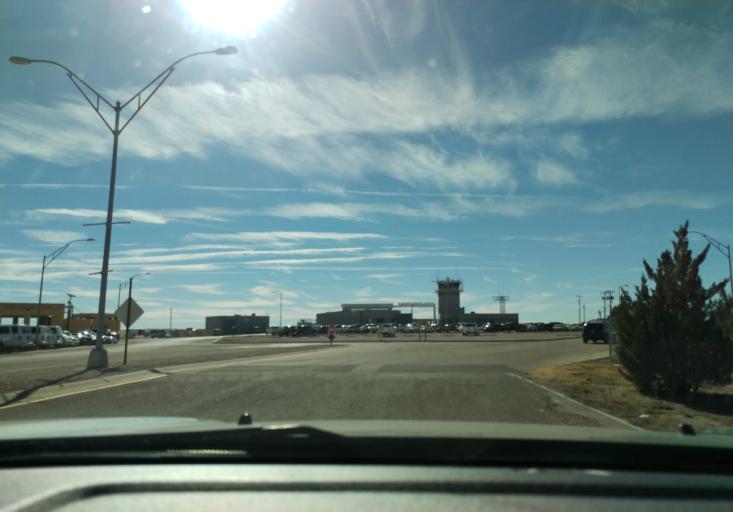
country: US
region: New Mexico
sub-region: Lea County
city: Hobbs
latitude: 32.6941
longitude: -103.2144
